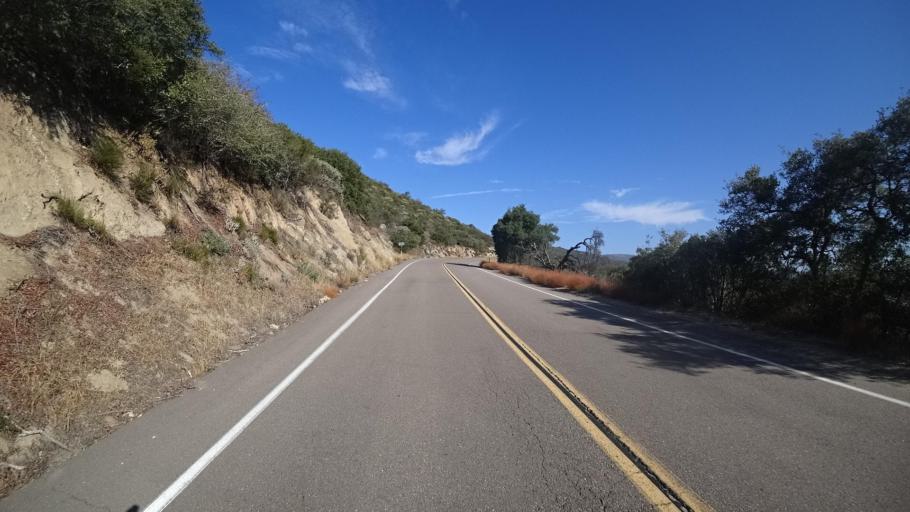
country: US
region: California
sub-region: Riverside County
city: Aguanga
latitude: 33.2578
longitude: -116.7625
